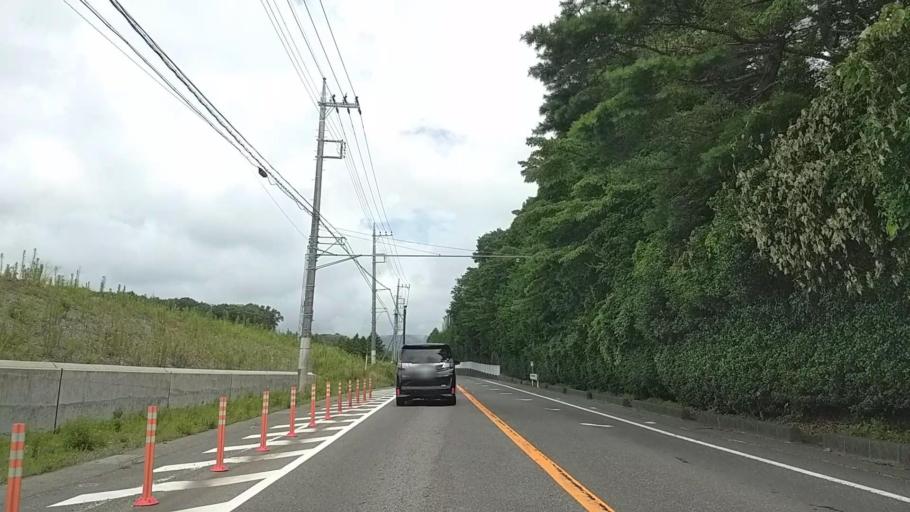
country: JP
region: Shizuoka
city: Gotemba
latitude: 35.3420
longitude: 138.8860
